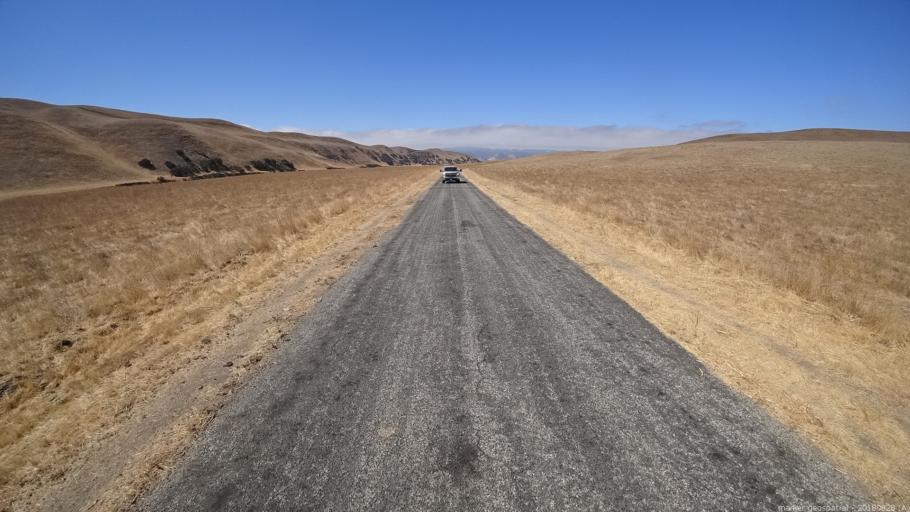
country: US
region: California
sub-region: San Luis Obispo County
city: Lake Nacimiento
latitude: 36.0379
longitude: -120.8426
